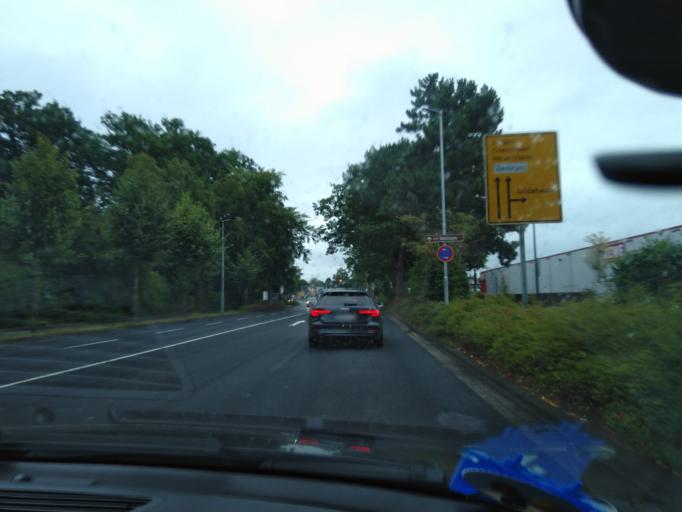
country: DE
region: Lower Saxony
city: Nordhorn
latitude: 52.4271
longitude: 7.0604
